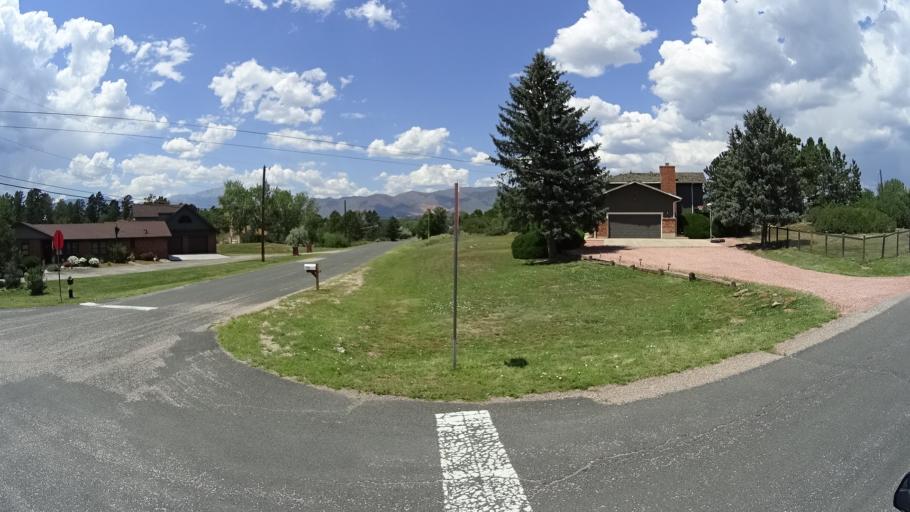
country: US
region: Colorado
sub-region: El Paso County
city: Air Force Academy
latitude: 38.9358
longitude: -104.8031
